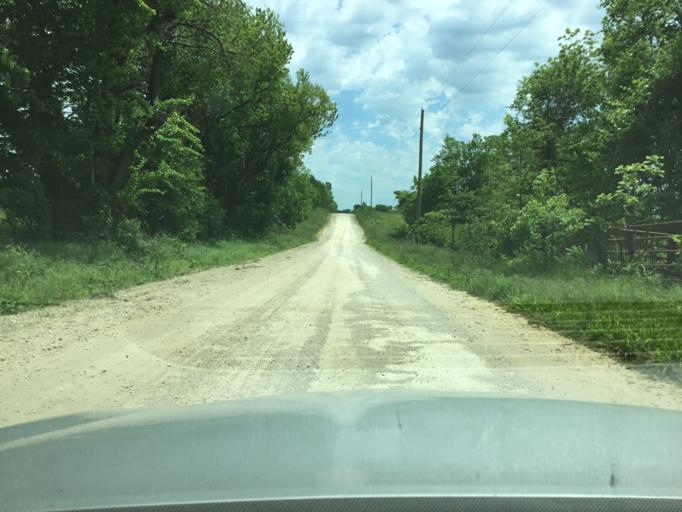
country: US
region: Kansas
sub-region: Montgomery County
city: Caney
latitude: 37.0953
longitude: -95.8151
